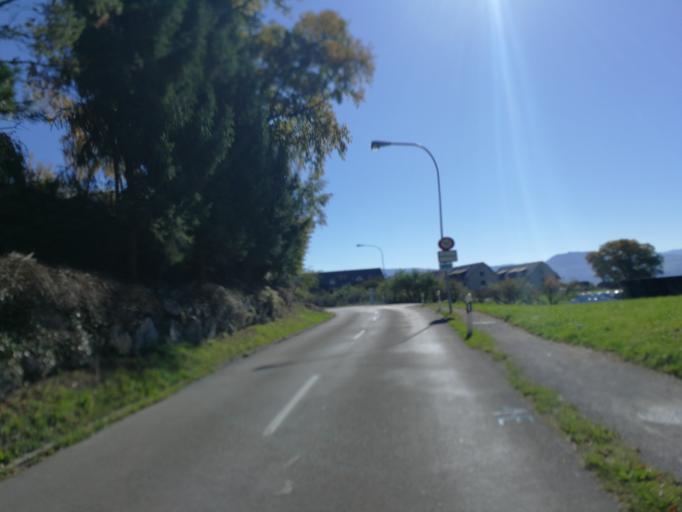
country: CH
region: Zurich
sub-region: Bezirk Hinwil
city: Wolfhausen
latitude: 47.2612
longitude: 8.7921
